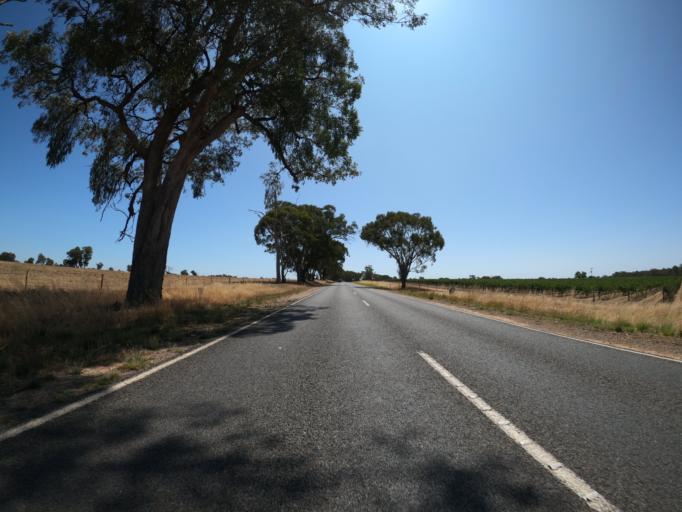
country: AU
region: Victoria
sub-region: Moira
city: Yarrawonga
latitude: -36.0678
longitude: 146.1839
